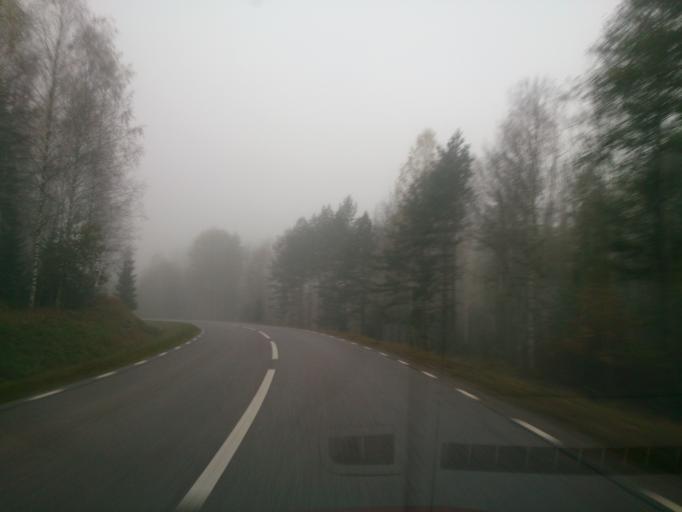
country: SE
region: OEstergoetland
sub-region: Atvidabergs Kommun
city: Atvidaberg
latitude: 58.0837
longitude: 15.9344
